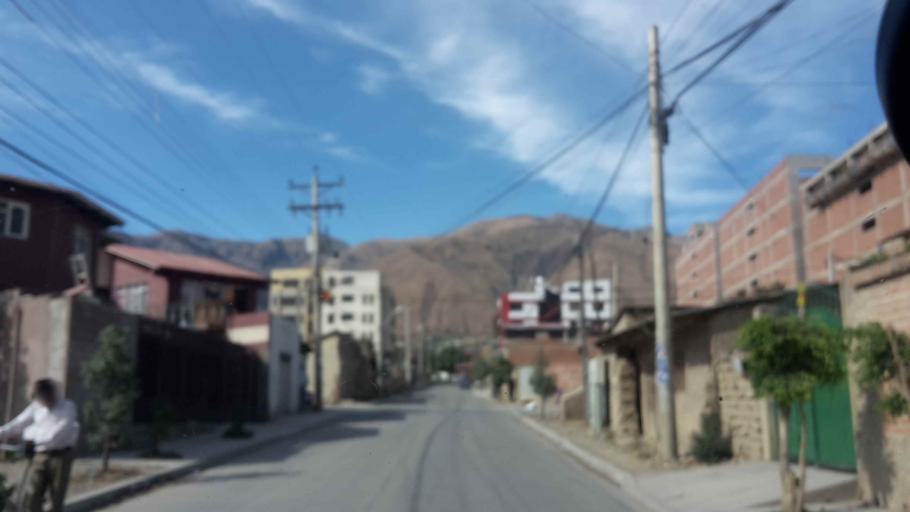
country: BO
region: Cochabamba
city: Cochabamba
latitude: -17.3468
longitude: -66.2047
